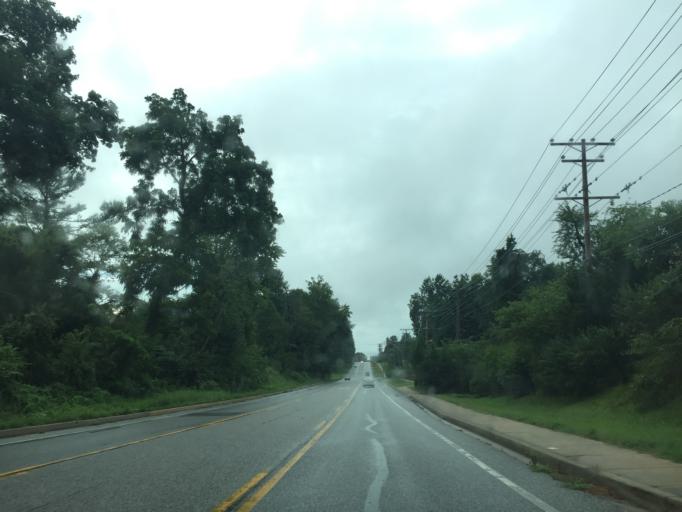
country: US
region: Maryland
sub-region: Harford County
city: South Bel Air
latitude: 39.5217
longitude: -76.3362
